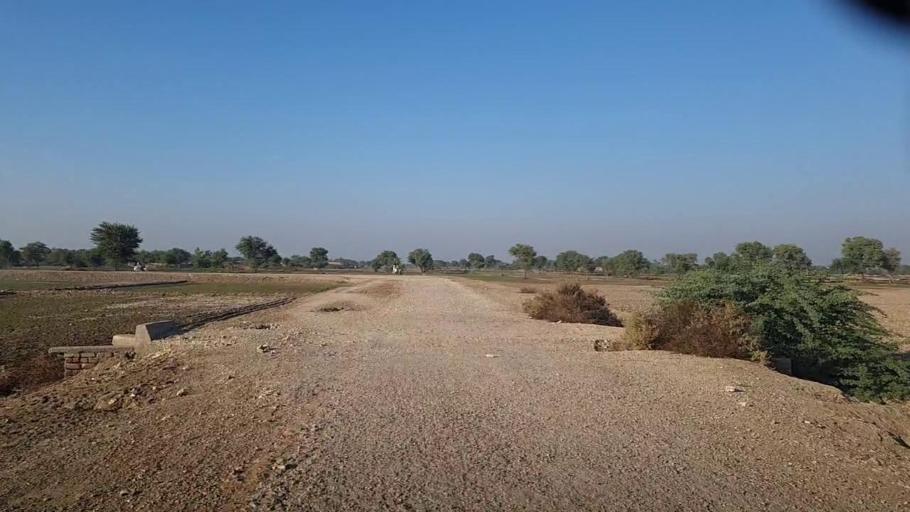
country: PK
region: Sindh
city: Pad Idan
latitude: 26.7333
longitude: 68.3492
